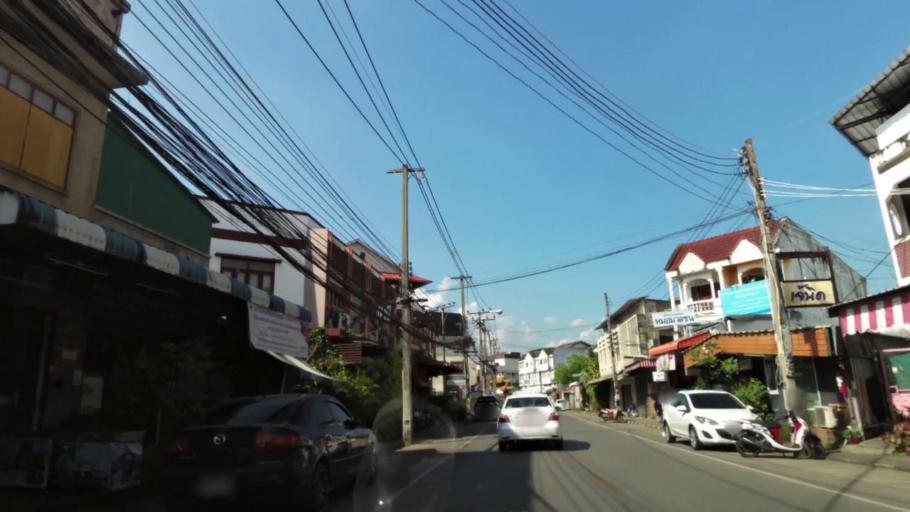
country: TH
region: Phrae
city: Phrae
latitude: 18.1396
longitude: 100.1432
